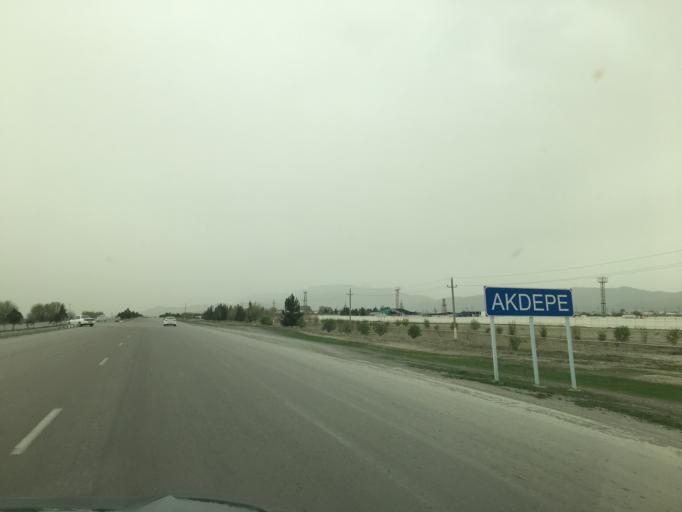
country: TM
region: Ahal
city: Baharly
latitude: 38.3257
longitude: 57.5879
